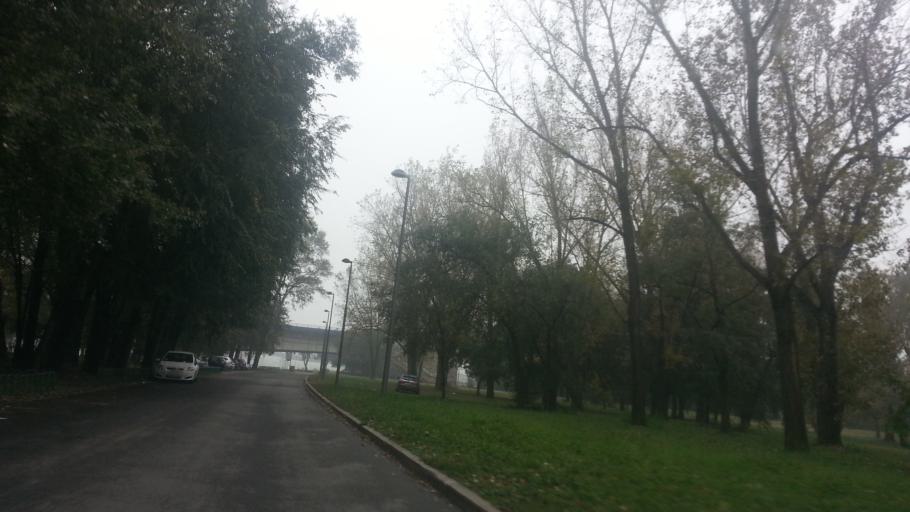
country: RS
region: Central Serbia
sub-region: Belgrade
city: Stari Grad
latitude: 44.8168
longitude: 20.4451
